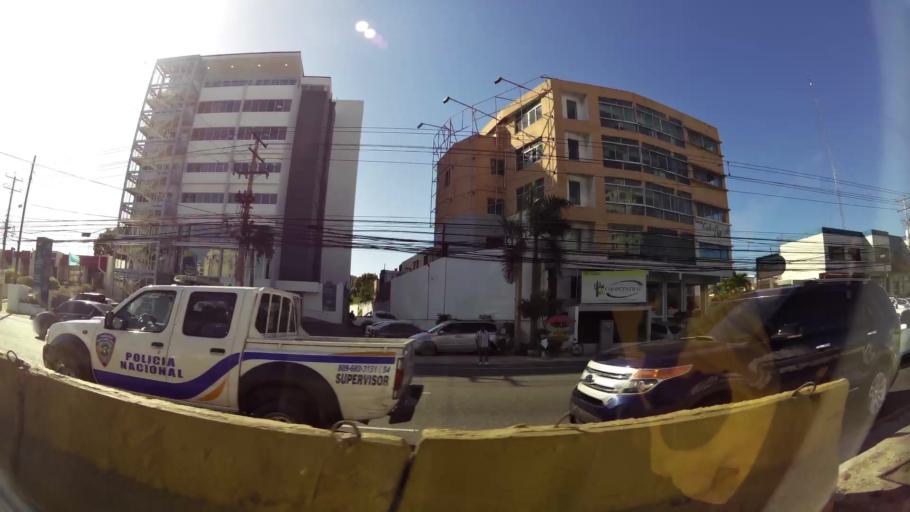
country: DO
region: Nacional
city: Bella Vista
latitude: 18.4593
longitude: -69.9428
